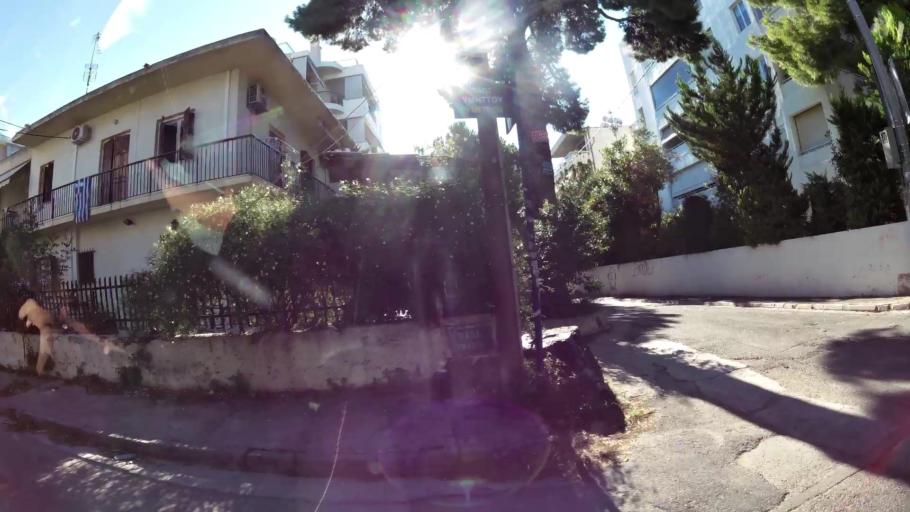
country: GR
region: Attica
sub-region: Nomarchia Athinas
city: Vrilissia
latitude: 38.0389
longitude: 23.8332
